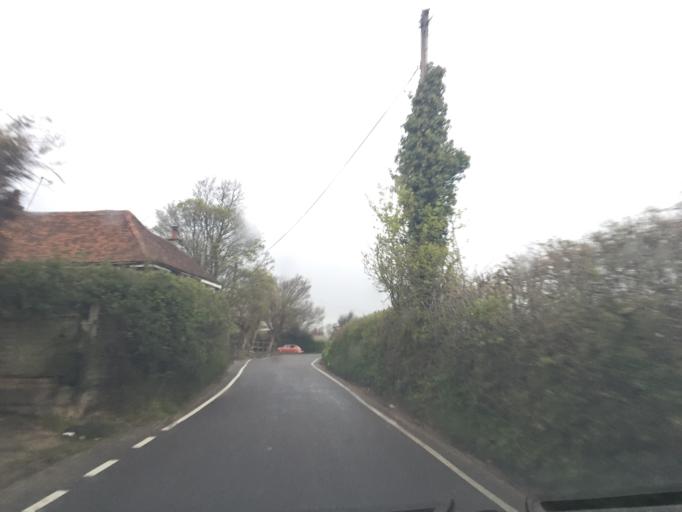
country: GB
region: England
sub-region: Essex
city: Harlow
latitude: 51.7390
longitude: 0.1003
